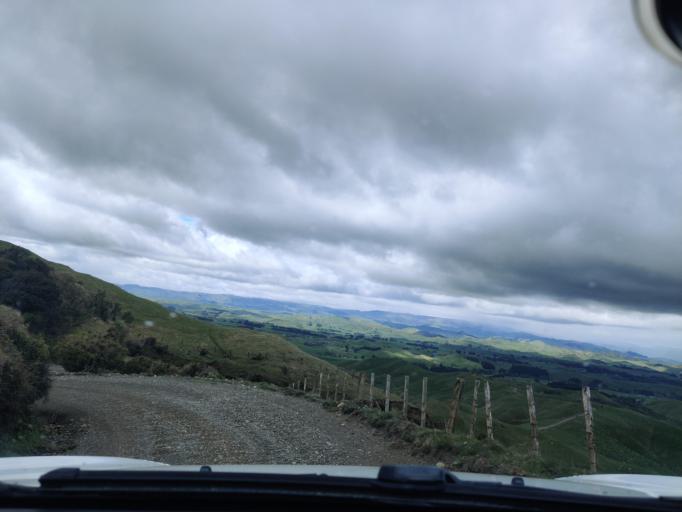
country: NZ
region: Manawatu-Wanganui
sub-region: Palmerston North City
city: Palmerston North
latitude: -40.2766
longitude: 175.8523
